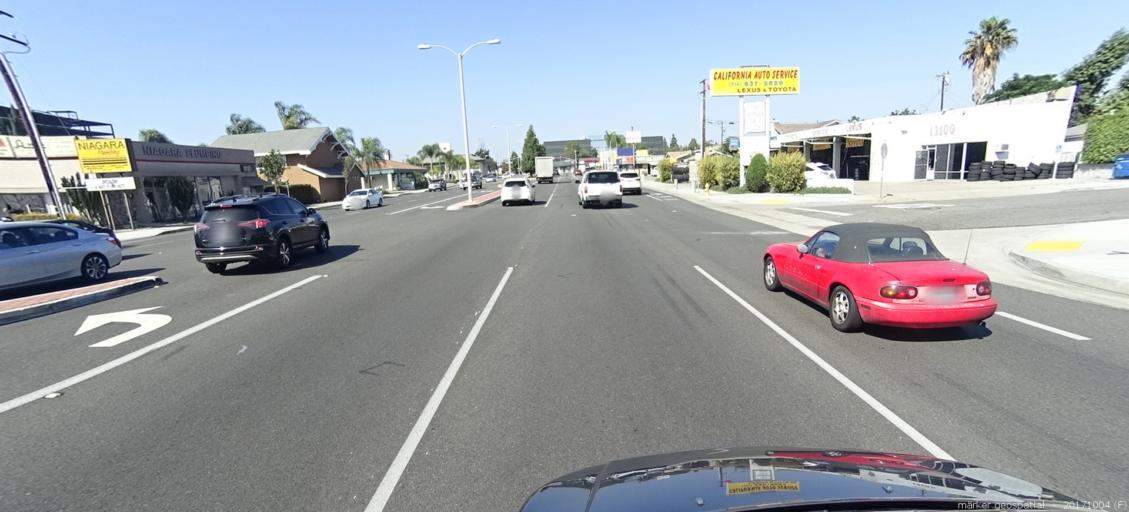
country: US
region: California
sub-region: Orange County
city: Garden Grove
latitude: 33.7720
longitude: -117.9549
